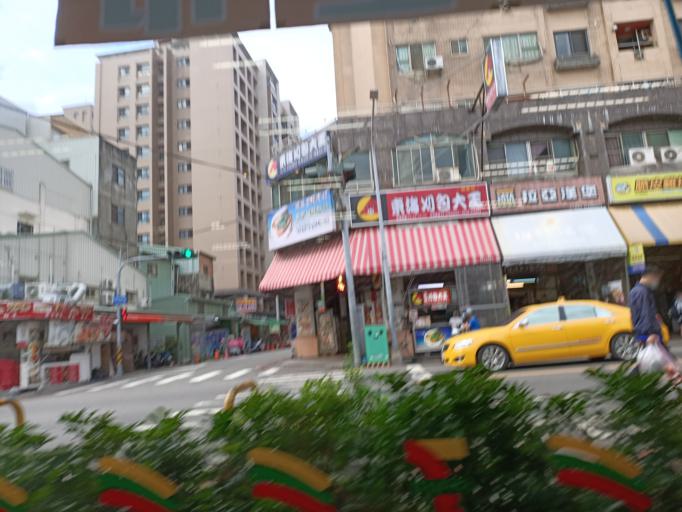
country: TW
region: Taiwan
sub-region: Taichung City
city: Taichung
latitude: 24.1384
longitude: 120.6114
